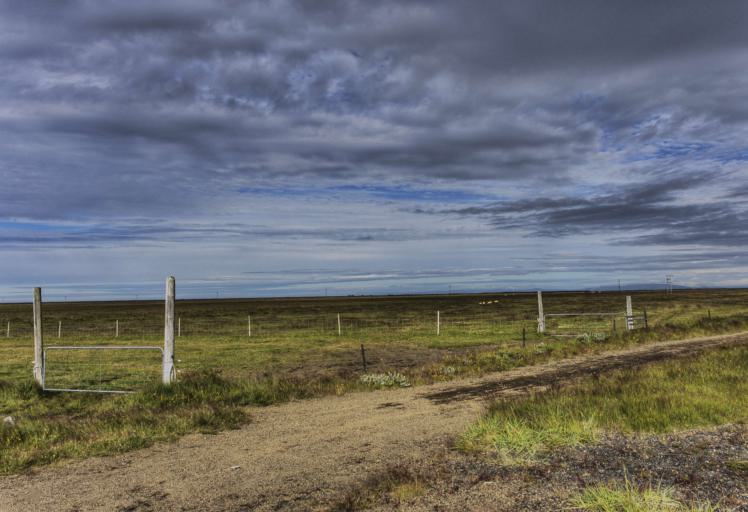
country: IS
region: South
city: Vestmannaeyjar
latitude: 63.7142
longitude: -20.2273
